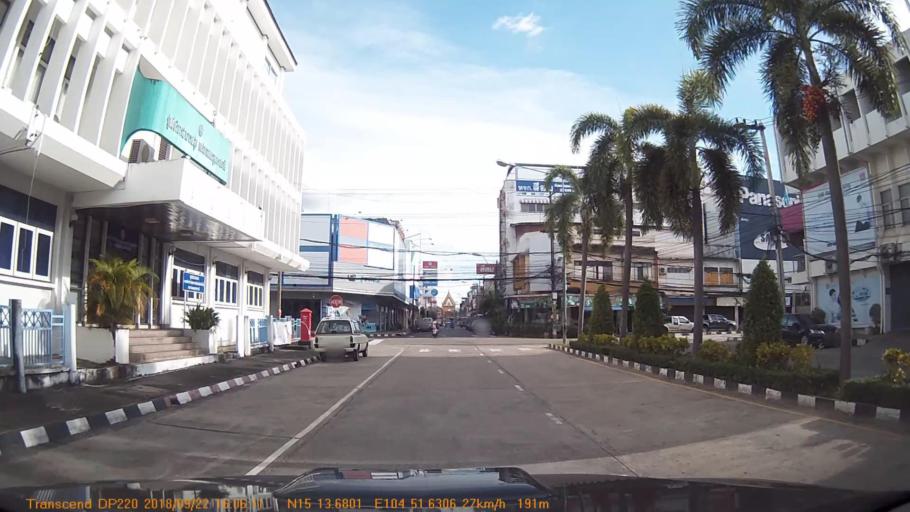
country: TH
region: Changwat Ubon Ratchathani
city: Ubon Ratchathani
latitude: 15.2280
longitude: 104.8605
